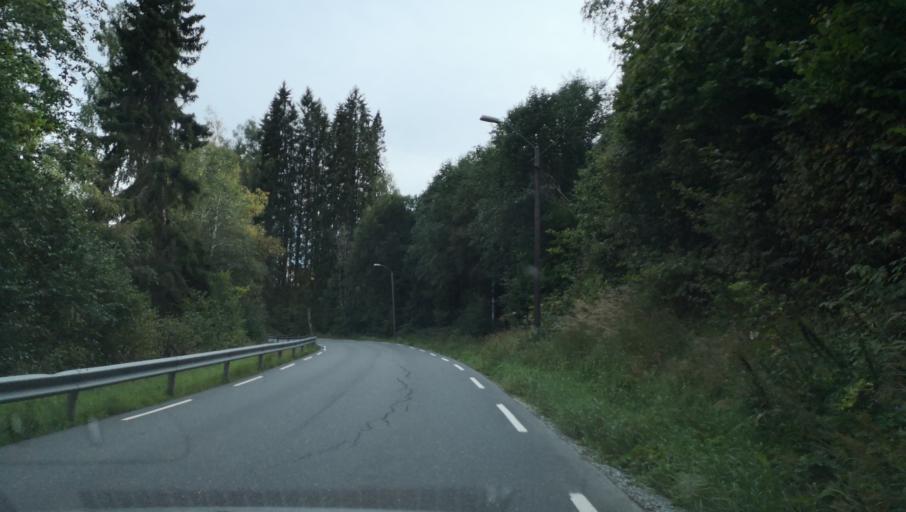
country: NO
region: Ostfold
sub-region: Hobol
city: Tomter
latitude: 59.6790
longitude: 11.0300
